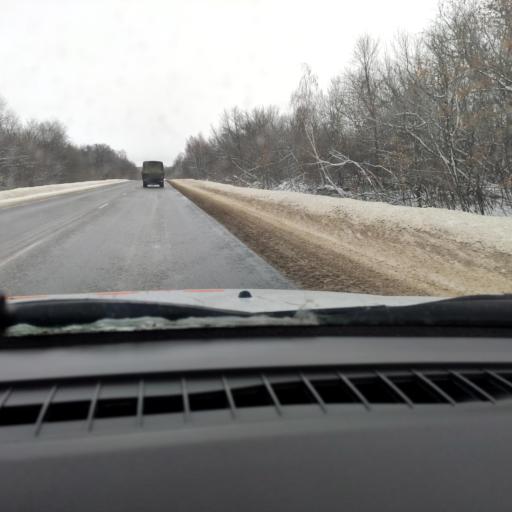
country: RU
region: Samara
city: Dubovyy Umet
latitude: 52.9568
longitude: 50.3004
